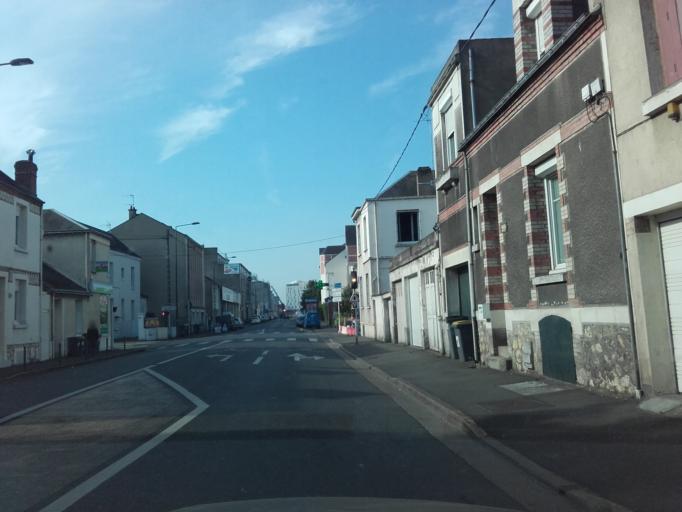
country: FR
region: Centre
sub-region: Departement d'Indre-et-Loire
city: Tours
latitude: 47.3802
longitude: 0.6774
